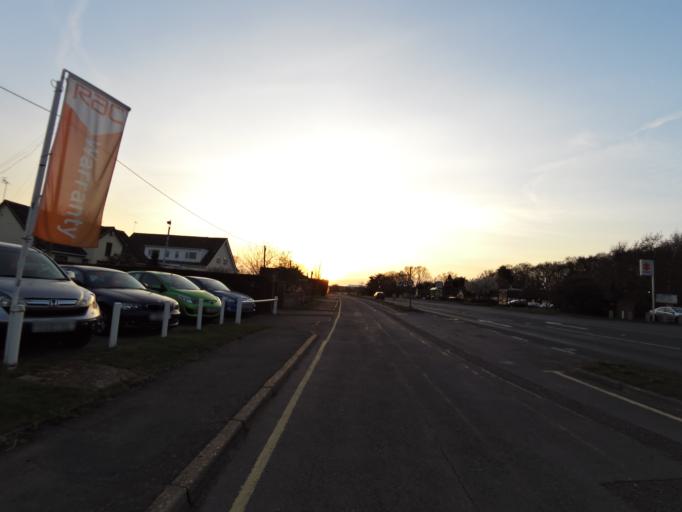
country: GB
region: England
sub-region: Suffolk
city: Kesgrave
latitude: 52.0276
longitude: 1.2324
